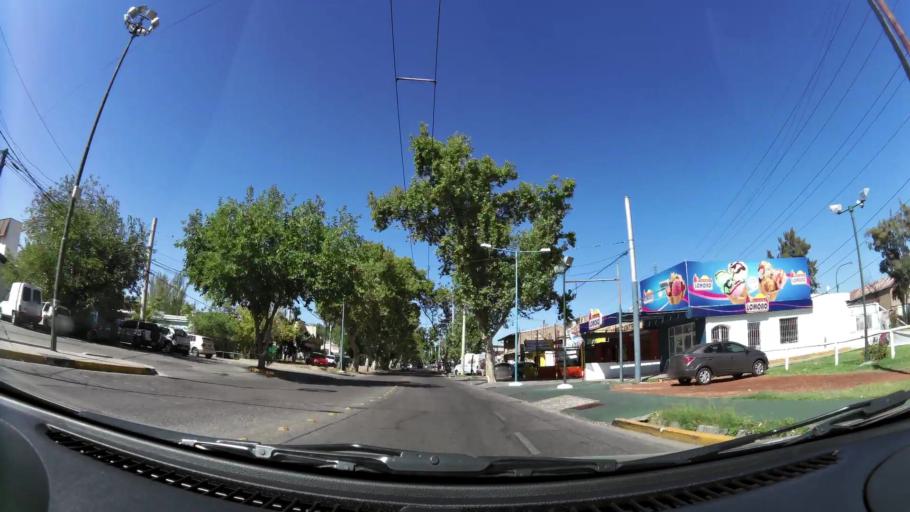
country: AR
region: Mendoza
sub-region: Departamento de Godoy Cruz
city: Godoy Cruz
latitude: -32.9393
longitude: -68.8414
